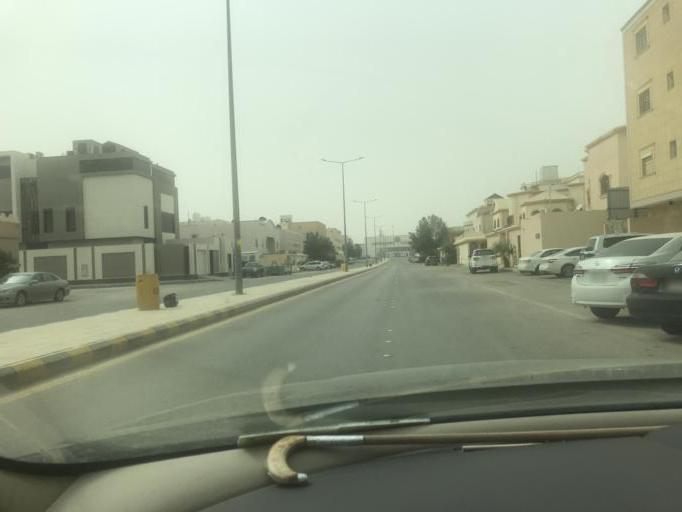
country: SA
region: Ar Riyad
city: Riyadh
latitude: 24.7315
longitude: 46.7955
